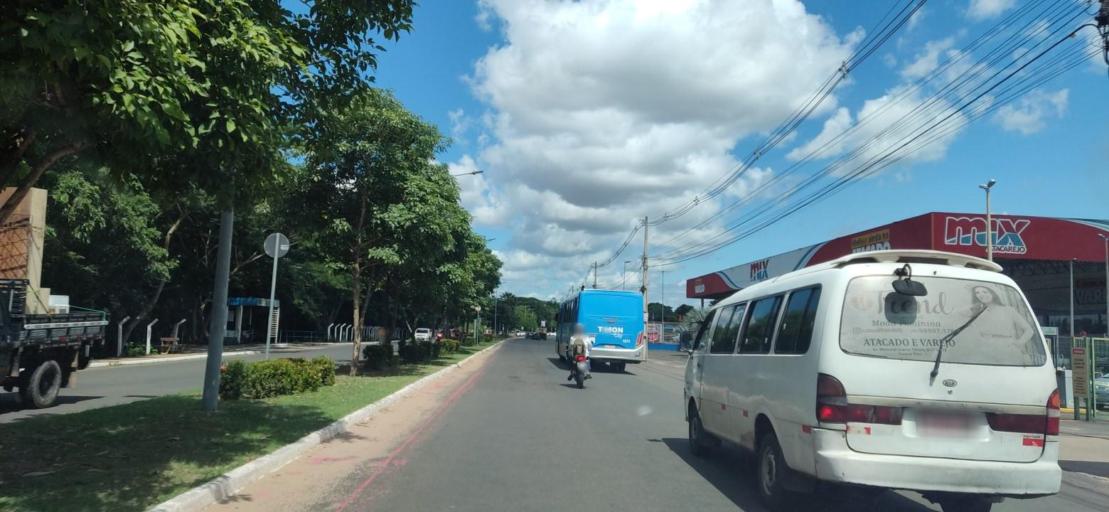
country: BR
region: Maranhao
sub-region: Timon
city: Timon
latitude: -5.0912
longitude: -42.8234
